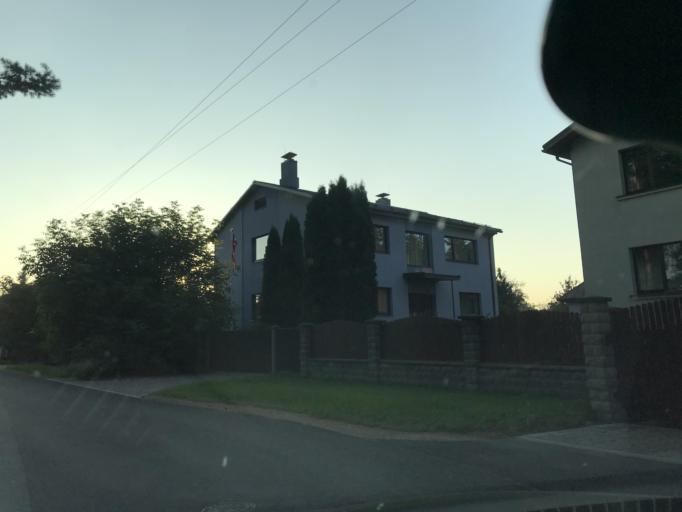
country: LV
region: Ikskile
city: Ikskile
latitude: 56.8270
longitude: 24.5072
